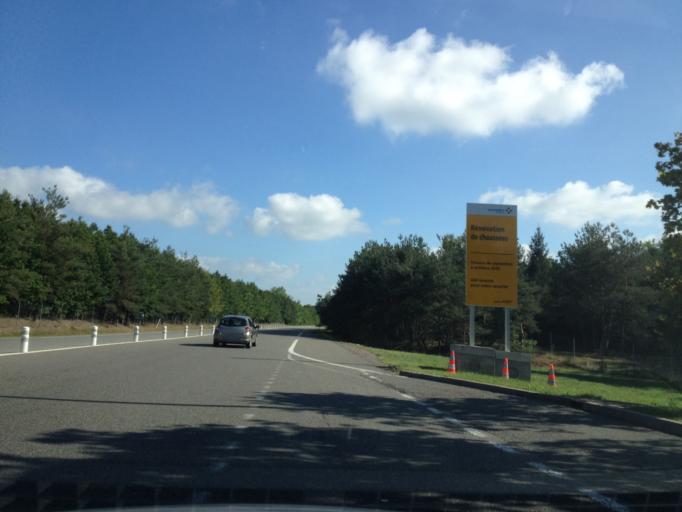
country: FR
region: Rhone-Alpes
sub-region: Departement de la Loire
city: Saint-Germain-Laval
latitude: 45.8607
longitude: 4.0424
